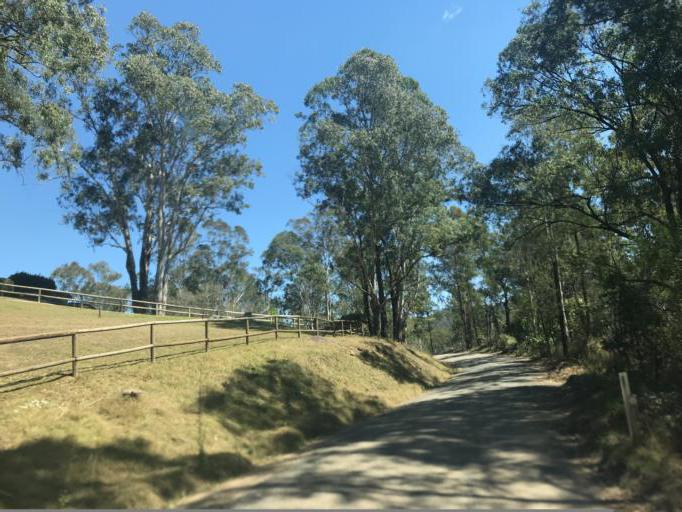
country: AU
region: New South Wales
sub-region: Hornsby Shire
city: Glenorie
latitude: -33.2591
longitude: 150.9736
